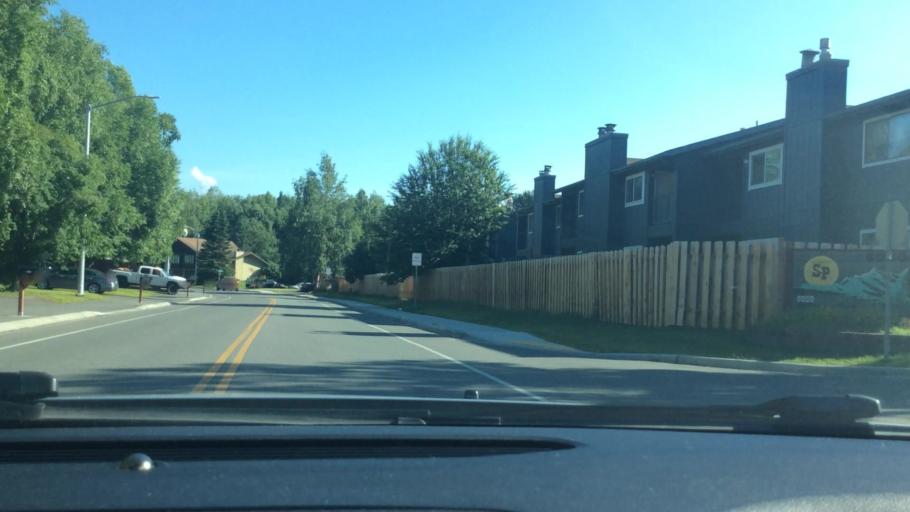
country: US
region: Alaska
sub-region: Anchorage Municipality
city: Elmendorf Air Force Base
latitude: 61.1846
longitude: -149.7306
